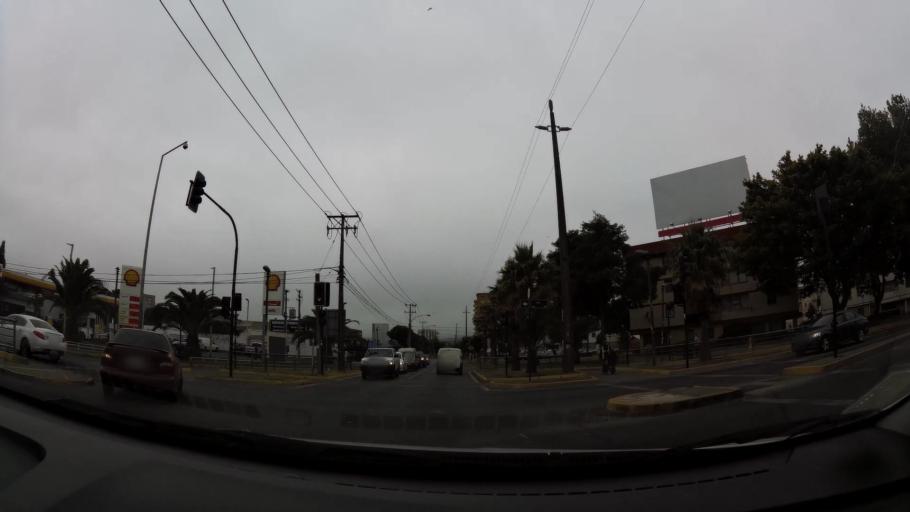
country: CL
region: Biobio
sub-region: Provincia de Concepcion
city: Concepcion
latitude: -36.8171
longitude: -73.0462
